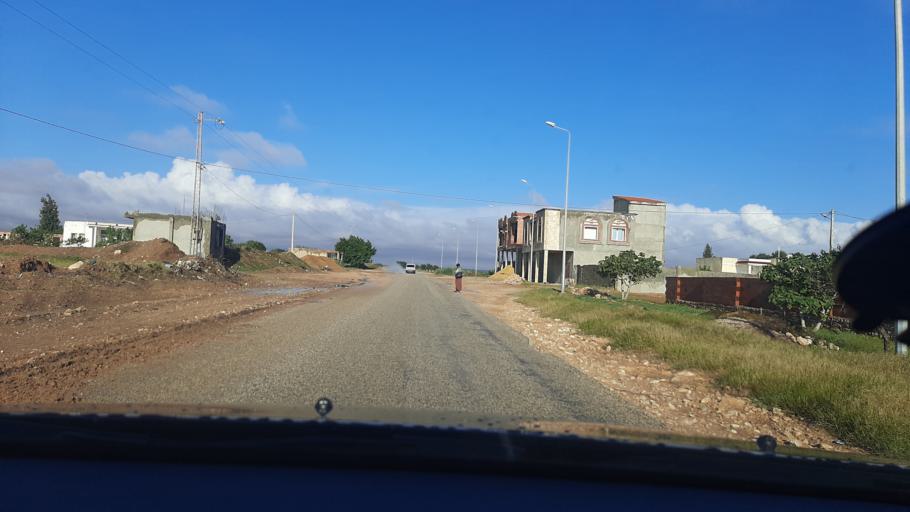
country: TN
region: Safaqis
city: Sfax
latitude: 34.8855
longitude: 10.6271
